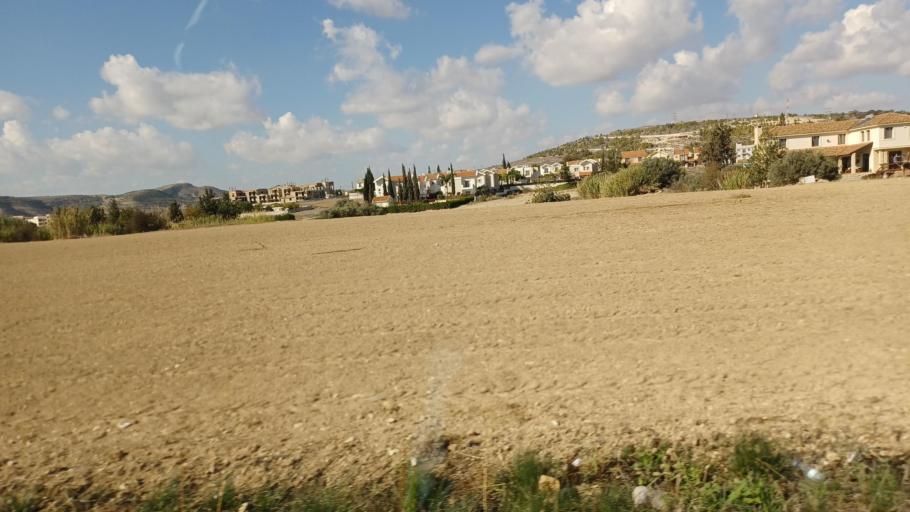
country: CY
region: Larnaka
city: Pyla
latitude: 34.9960
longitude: 33.6848
